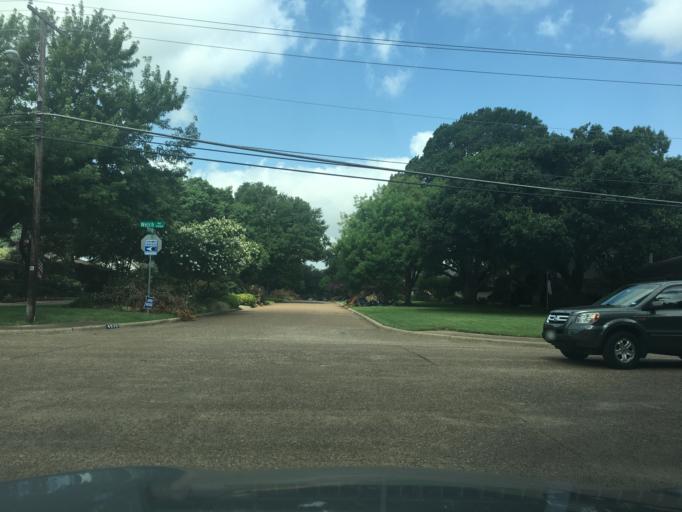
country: US
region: Texas
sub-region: Dallas County
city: Addison
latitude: 32.9132
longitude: -96.8294
